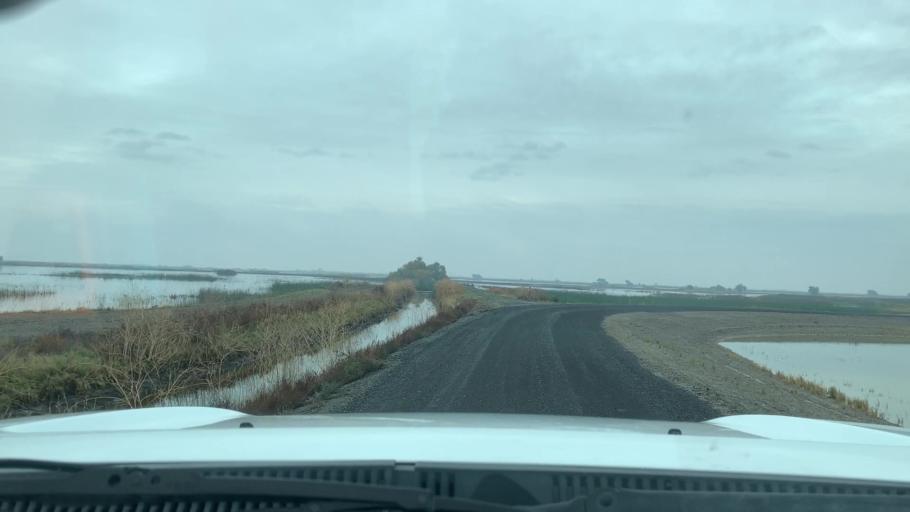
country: US
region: California
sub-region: Kern County
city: Lost Hills
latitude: 35.7372
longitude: -119.6105
